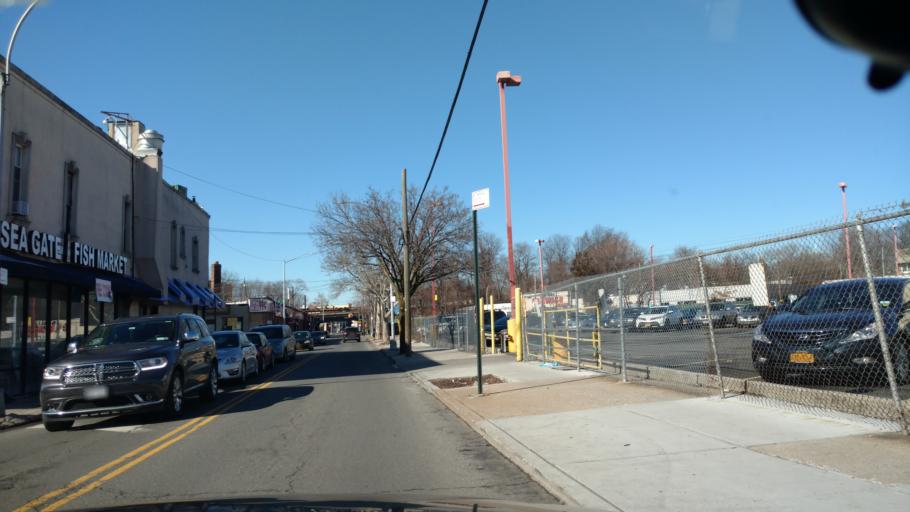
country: US
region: New York
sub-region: Kings County
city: East New York
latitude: 40.7012
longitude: -73.8909
